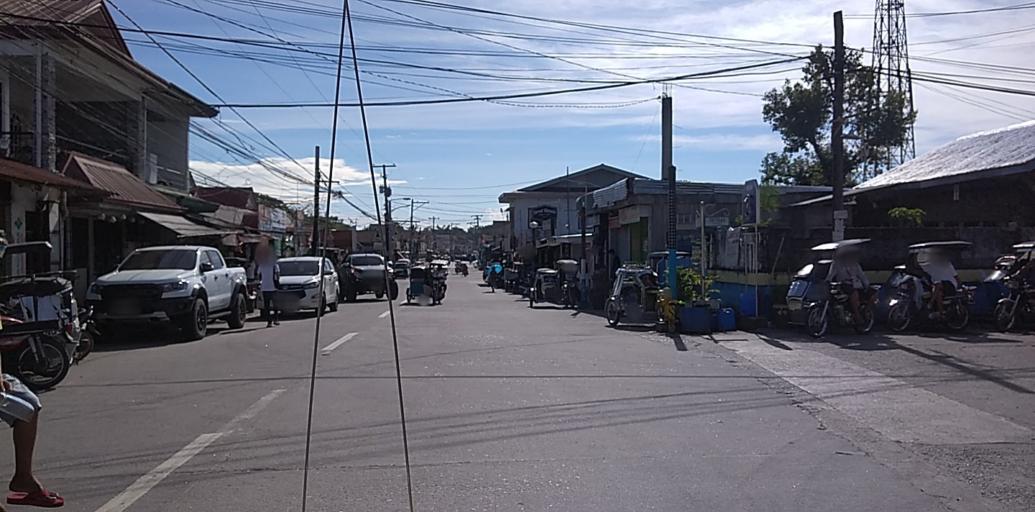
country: PH
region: Central Luzon
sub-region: Province of Pampanga
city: Porac
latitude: 15.0731
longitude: 120.5407
